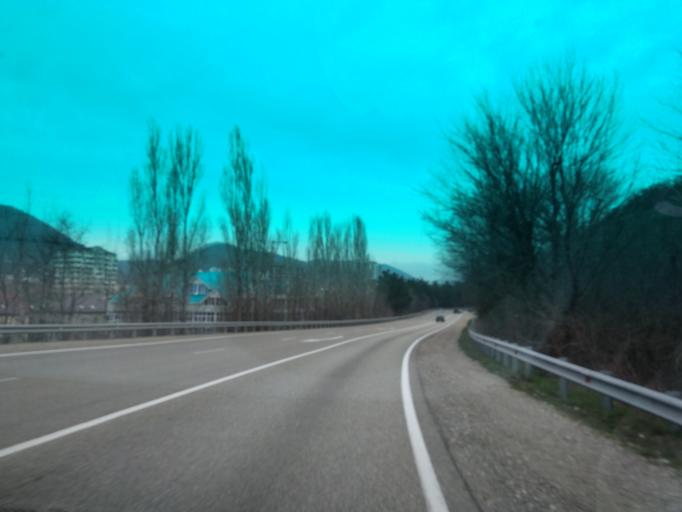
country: RU
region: Krasnodarskiy
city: Ol'ginka
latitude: 44.1911
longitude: 38.8889
